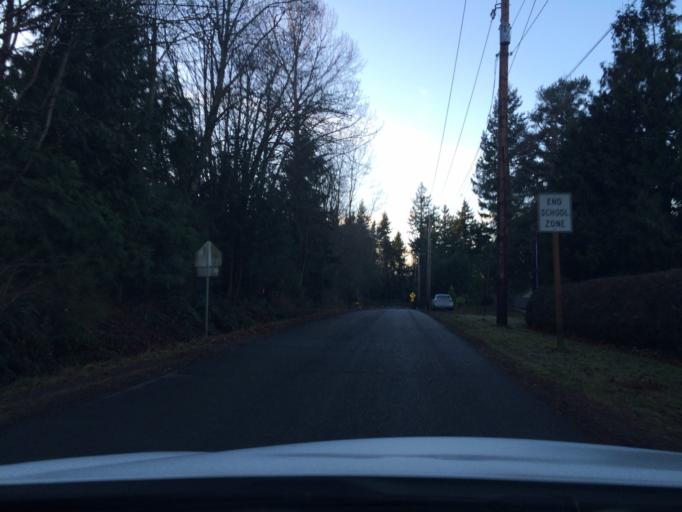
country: US
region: Washington
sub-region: Whatcom County
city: Geneva
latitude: 48.7489
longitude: -122.4043
